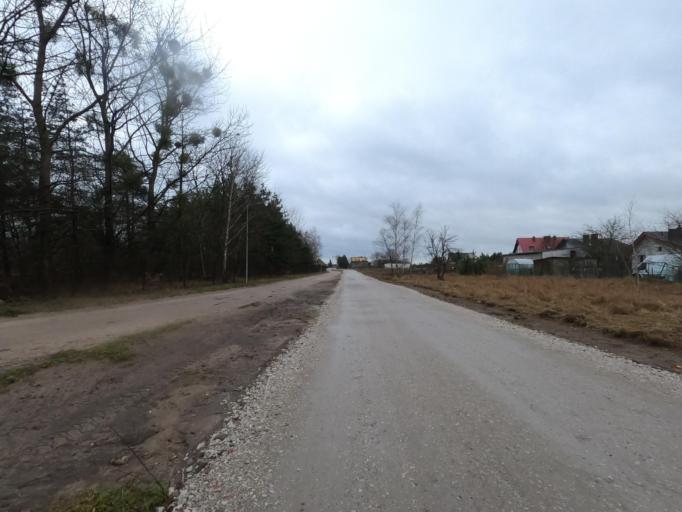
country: PL
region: Greater Poland Voivodeship
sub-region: Powiat pilski
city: Osiek nad Notecia
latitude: 53.1239
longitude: 17.2973
